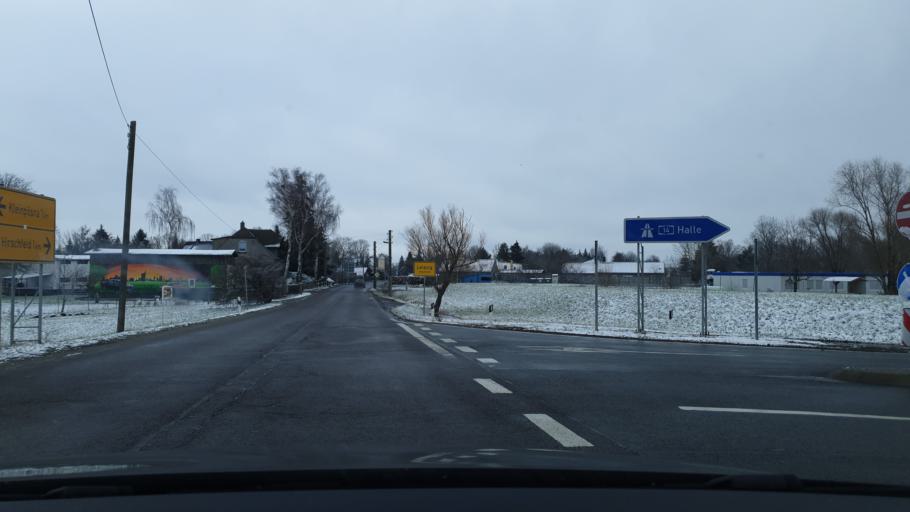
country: DE
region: Saxony
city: Borsdorf
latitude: 51.3204
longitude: 12.5233
